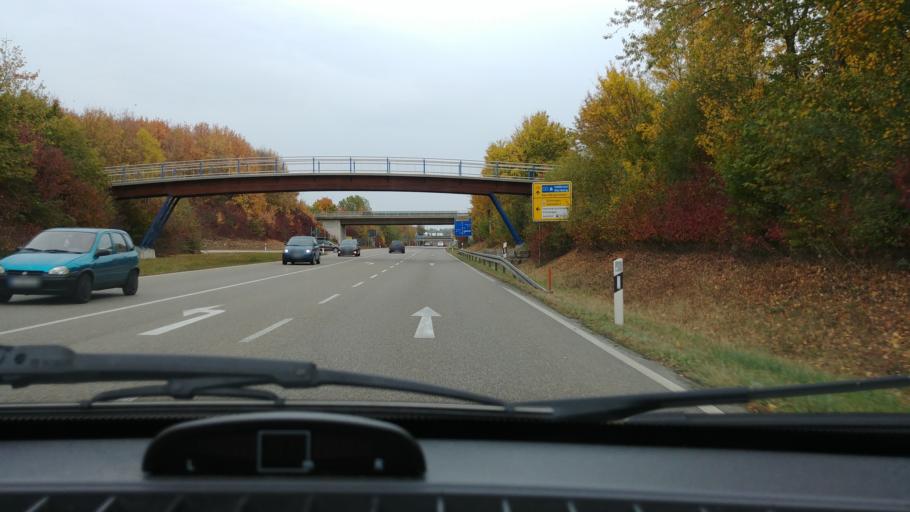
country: DE
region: Baden-Wuerttemberg
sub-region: Regierungsbezirk Stuttgart
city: Satteldorf
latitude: 49.1790
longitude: 10.0698
